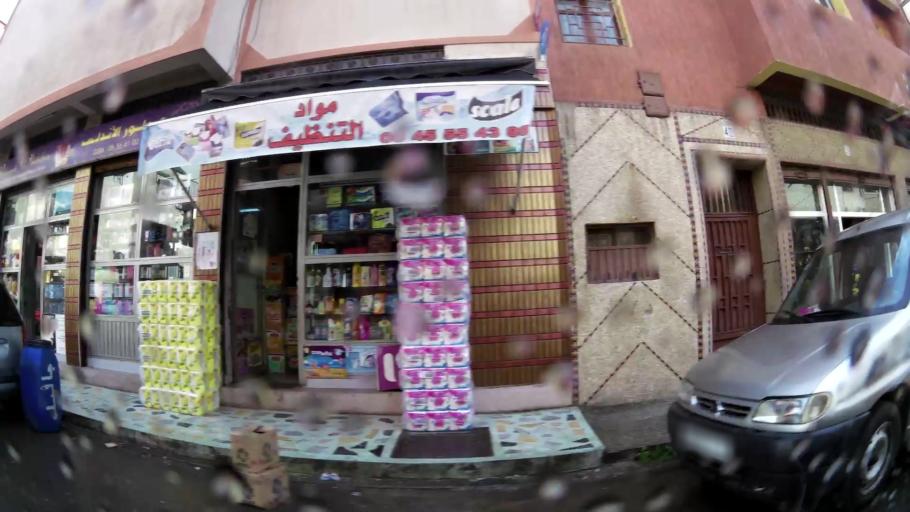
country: MA
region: Grand Casablanca
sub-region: Casablanca
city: Casablanca
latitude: 33.5469
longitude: -7.5986
